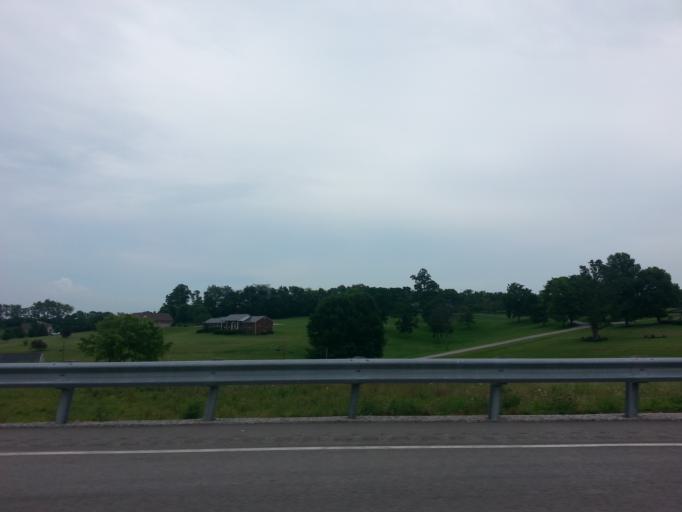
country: US
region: Ohio
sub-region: Brown County
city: Aberdeen
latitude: 38.6256
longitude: -83.8376
